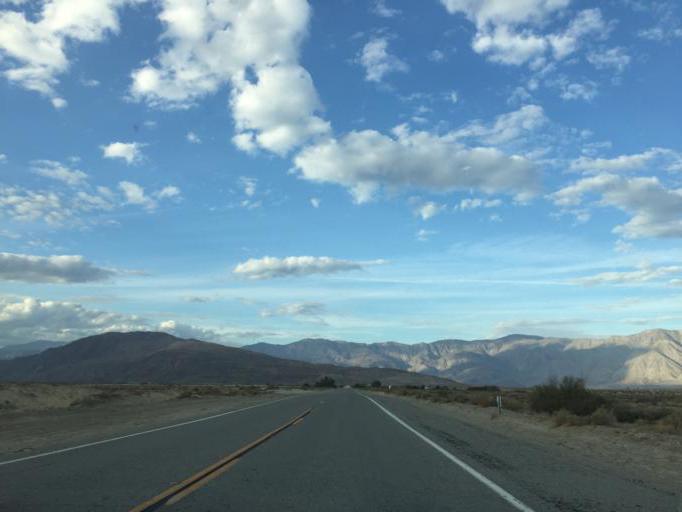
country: US
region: California
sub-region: San Diego County
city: Borrego Springs
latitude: 33.2623
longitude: -116.2989
